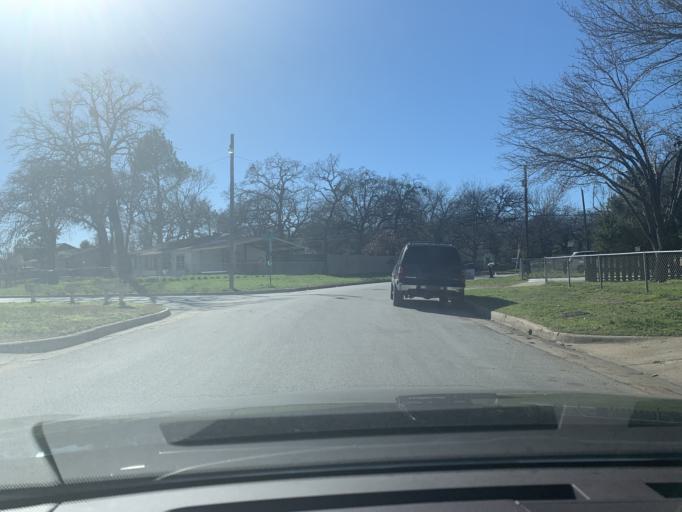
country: US
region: Texas
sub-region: Tarrant County
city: Haltom City
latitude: 32.7695
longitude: -97.2842
